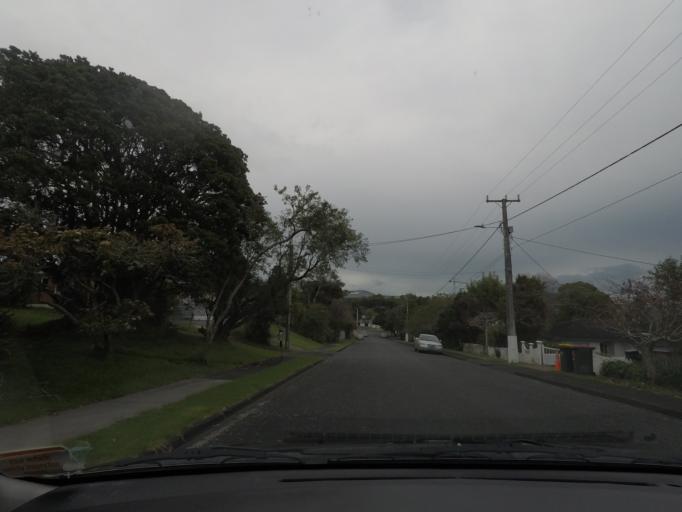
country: NZ
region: Auckland
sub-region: Auckland
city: Rosebank
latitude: -36.8577
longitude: 174.6413
